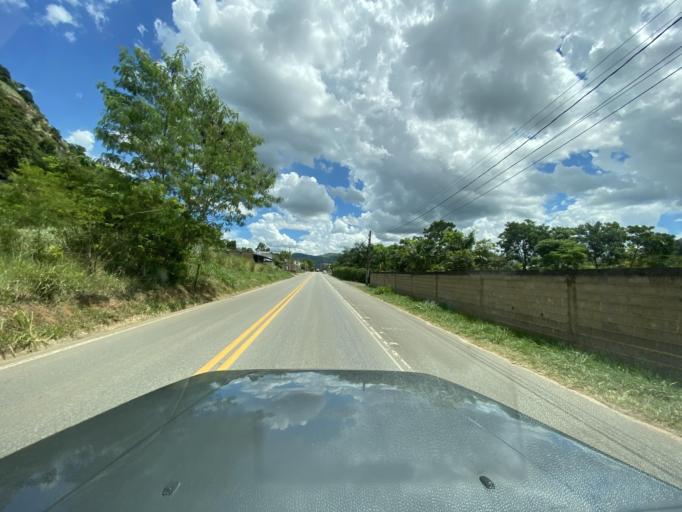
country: BR
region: Espirito Santo
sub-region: Jeronimo Monteiro
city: Jeronimo Monteiro
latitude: -20.7926
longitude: -41.3961
